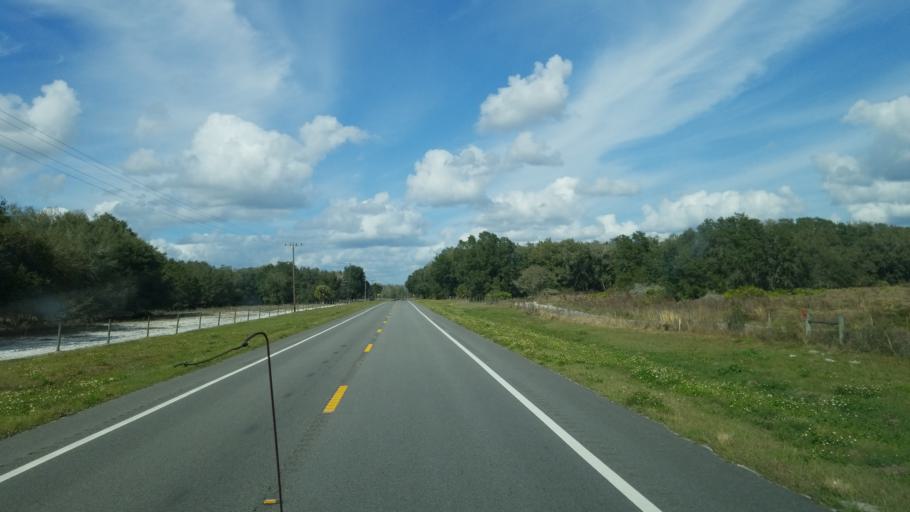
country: US
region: Florida
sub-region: Brevard County
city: June Park
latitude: 27.9353
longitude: -80.9960
